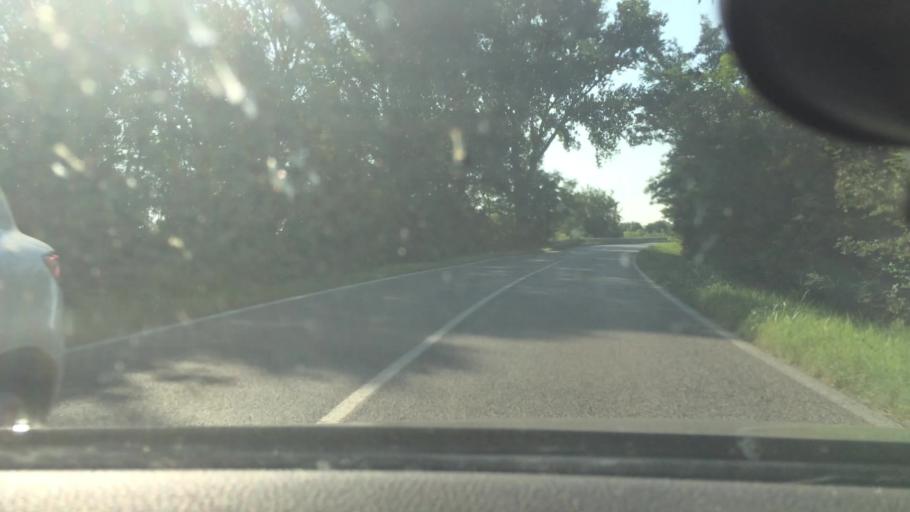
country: IT
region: Emilia-Romagna
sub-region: Provincia di Ferrara
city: Lagosanto
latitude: 44.7456
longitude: 12.1405
